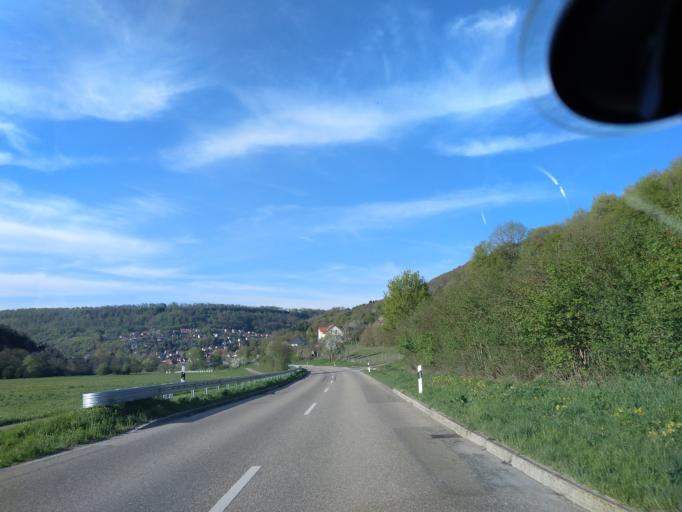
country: DE
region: Baden-Wuerttemberg
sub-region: Regierungsbezirk Stuttgart
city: Braunsbach
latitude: 49.1893
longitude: 9.7926
